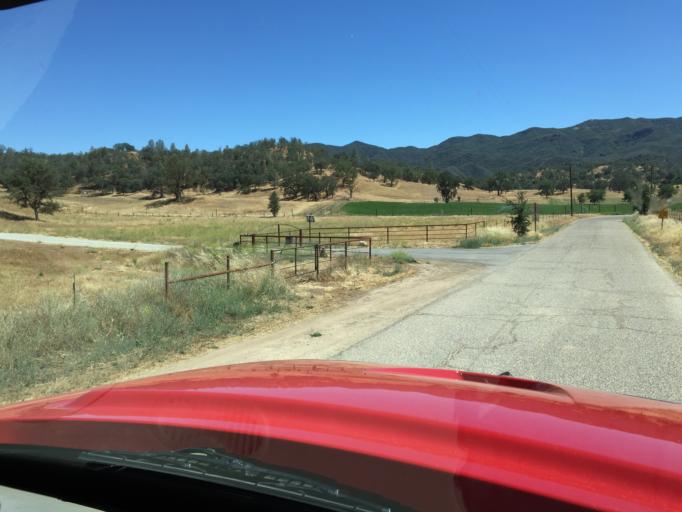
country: US
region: California
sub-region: San Luis Obispo County
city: Santa Margarita
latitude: 35.3048
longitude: -120.3674
